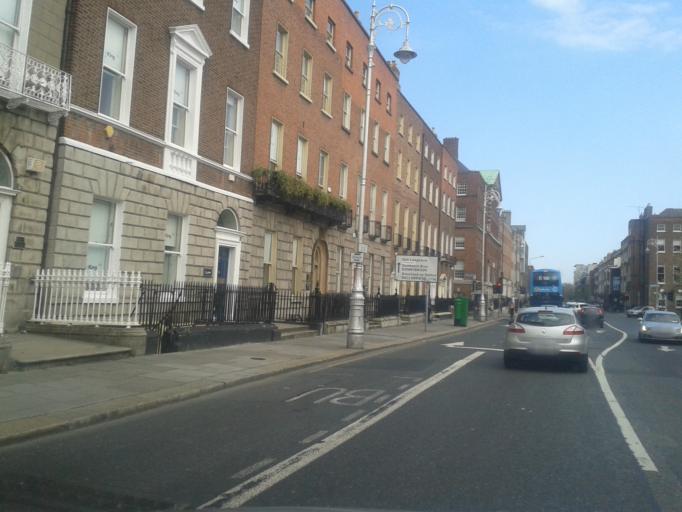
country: IE
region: Leinster
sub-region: Dublin City
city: Dublin
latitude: 53.3401
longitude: -6.2477
